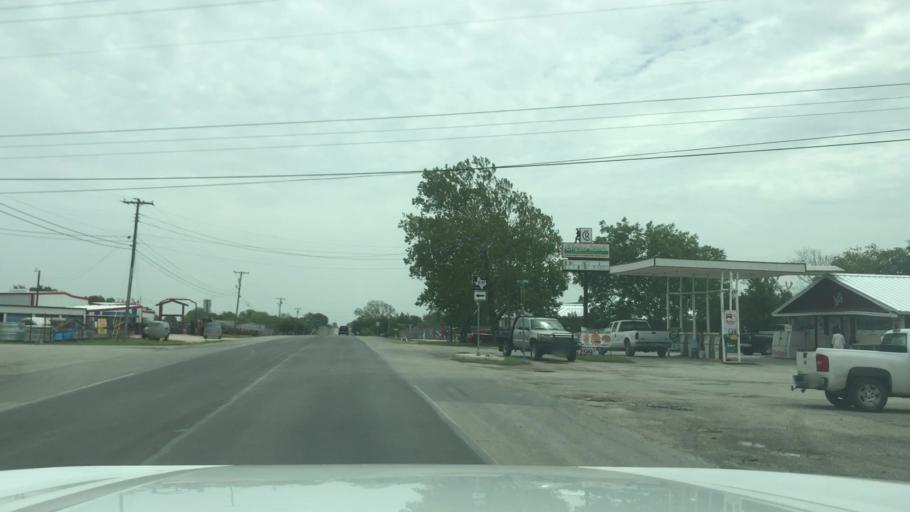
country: US
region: Texas
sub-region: Erath County
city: Dublin
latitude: 32.0832
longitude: -98.3327
